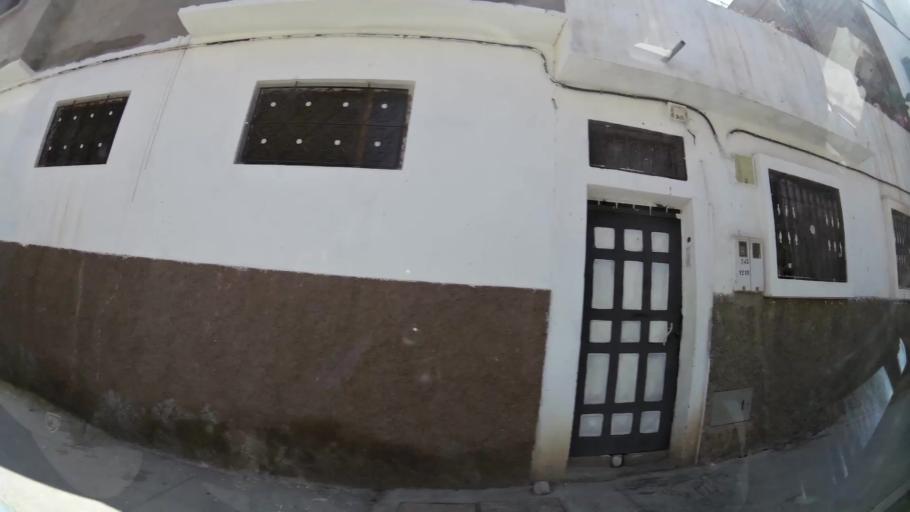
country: MA
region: Oued ed Dahab-Lagouira
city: Dakhla
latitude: 30.4403
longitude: -9.5534
